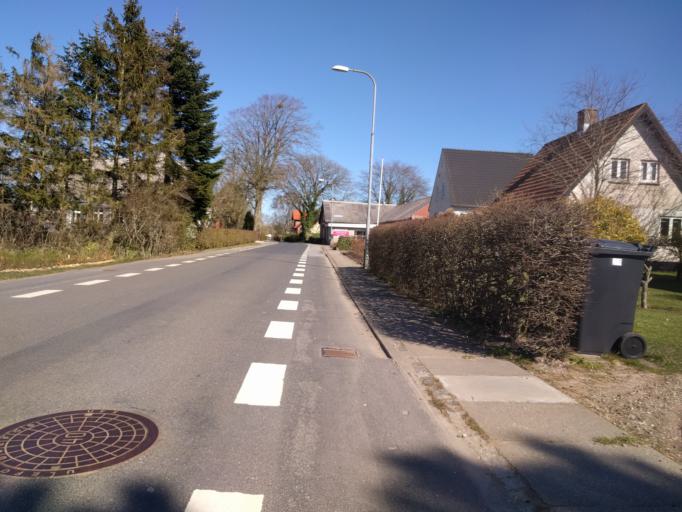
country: DK
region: South Denmark
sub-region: Kerteminde Kommune
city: Langeskov
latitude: 55.3796
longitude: 10.5617
